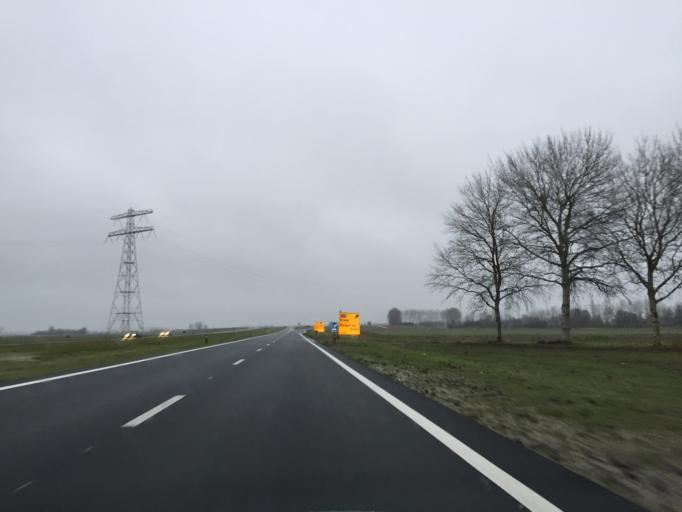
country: NL
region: Zeeland
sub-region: Gemeente Borsele
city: Borssele
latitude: 51.4822
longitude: 3.7869
